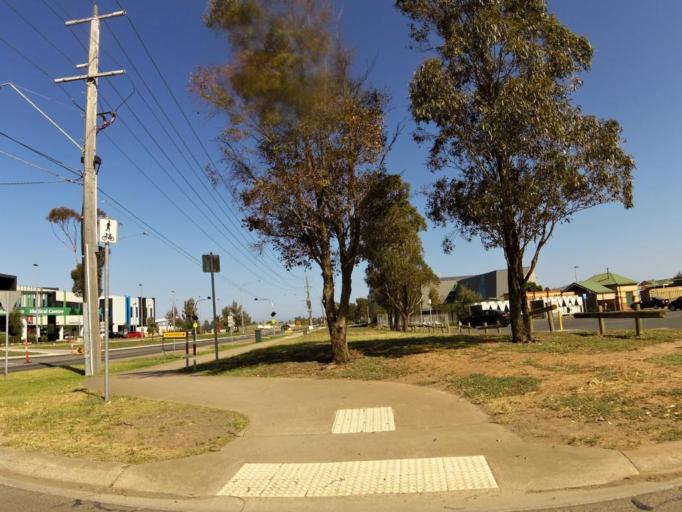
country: AU
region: Victoria
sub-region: Wyndham
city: Hoppers Crossing
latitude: -37.8858
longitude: 144.7002
